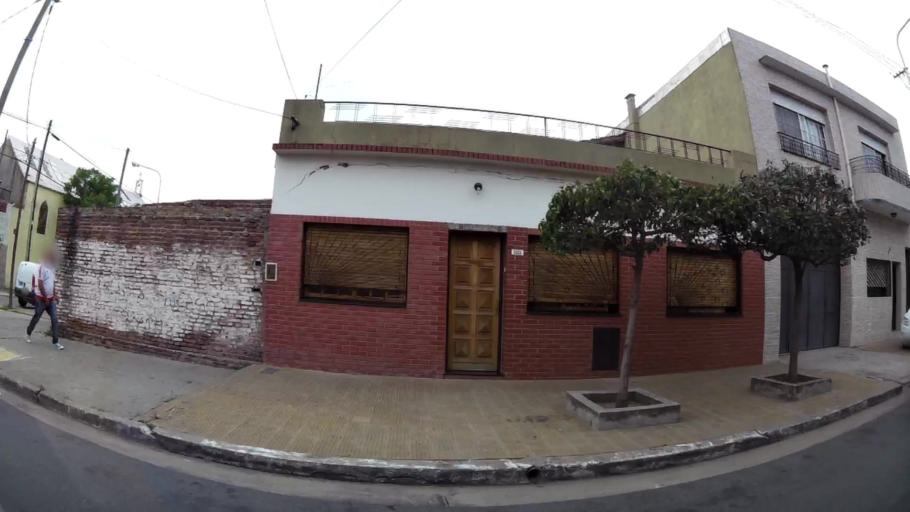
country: AR
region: Buenos Aires F.D.
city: Villa Lugano
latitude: -34.6713
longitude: -58.5118
